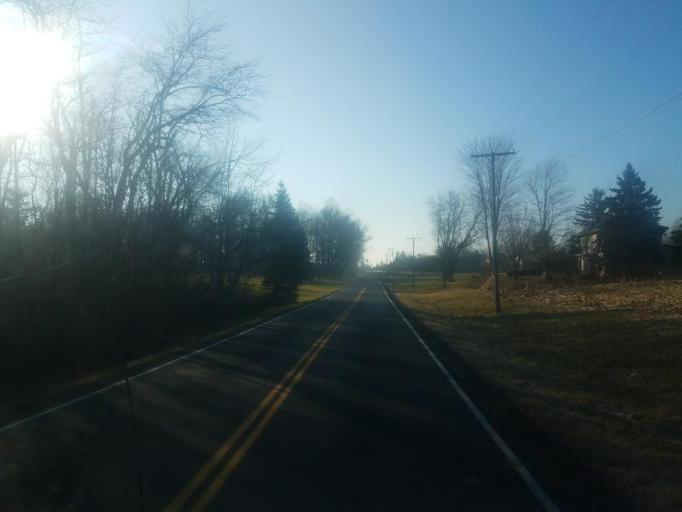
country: US
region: Ohio
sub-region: Crawford County
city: Bucyrus
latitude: 40.8231
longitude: -82.9402
